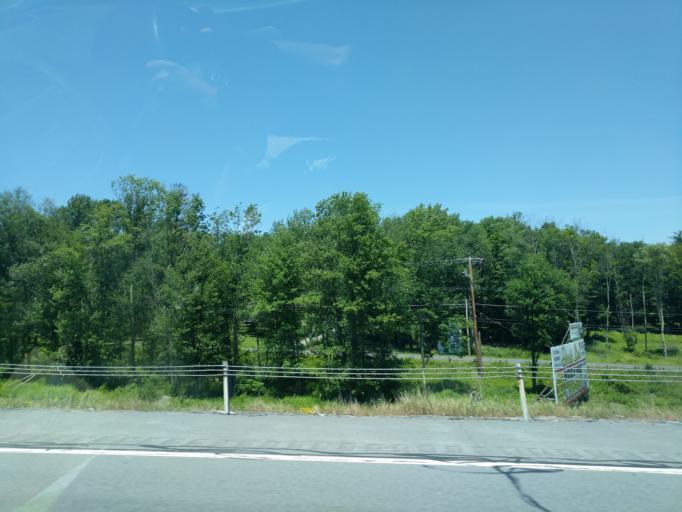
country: US
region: New York
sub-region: Sullivan County
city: Rock Hill
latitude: 41.6403
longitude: -74.6362
